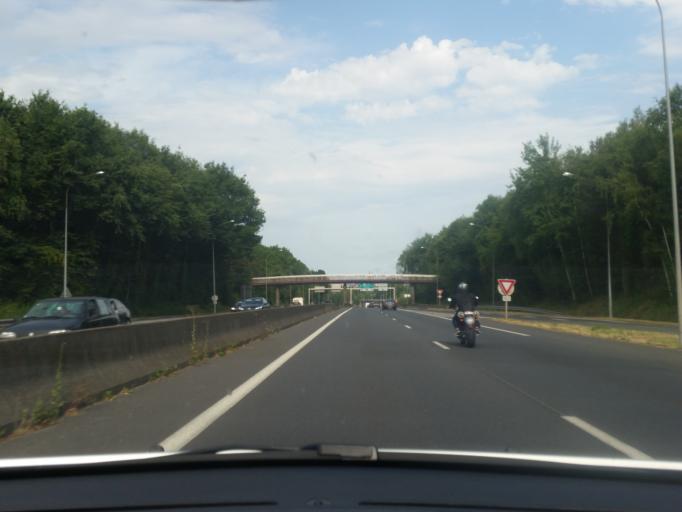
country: FR
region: Pays de la Loire
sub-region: Departement de Maine-et-Loire
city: Beaucouze
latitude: 47.4693
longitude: -0.5999
